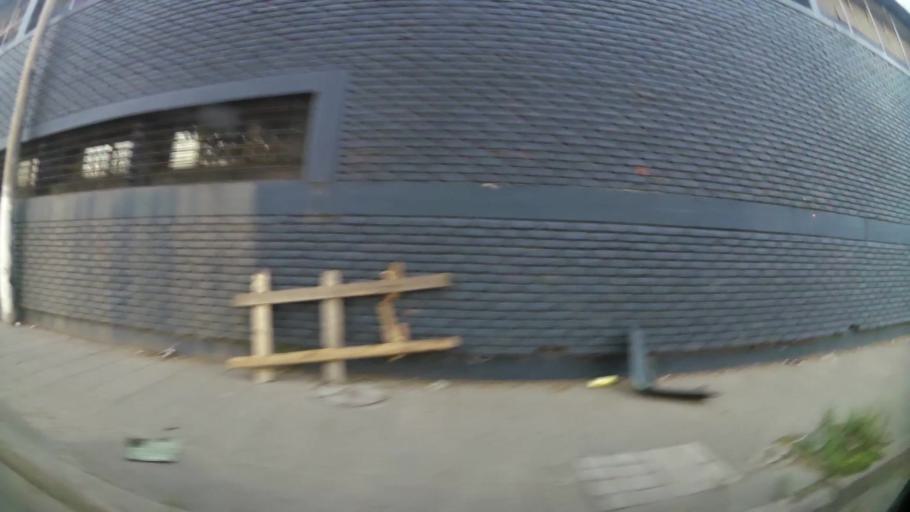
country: AR
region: Cordoba
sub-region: Departamento de Capital
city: Cordoba
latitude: -31.3957
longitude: -64.2021
